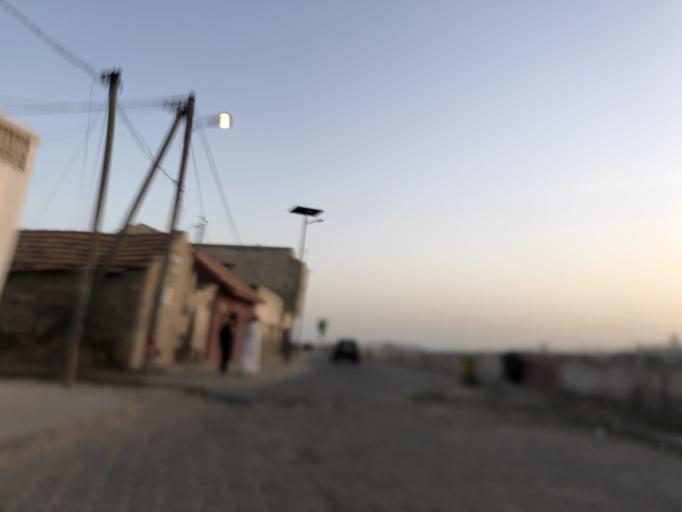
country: SN
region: Saint-Louis
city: Saint-Louis
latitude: 16.0208
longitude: -16.5067
